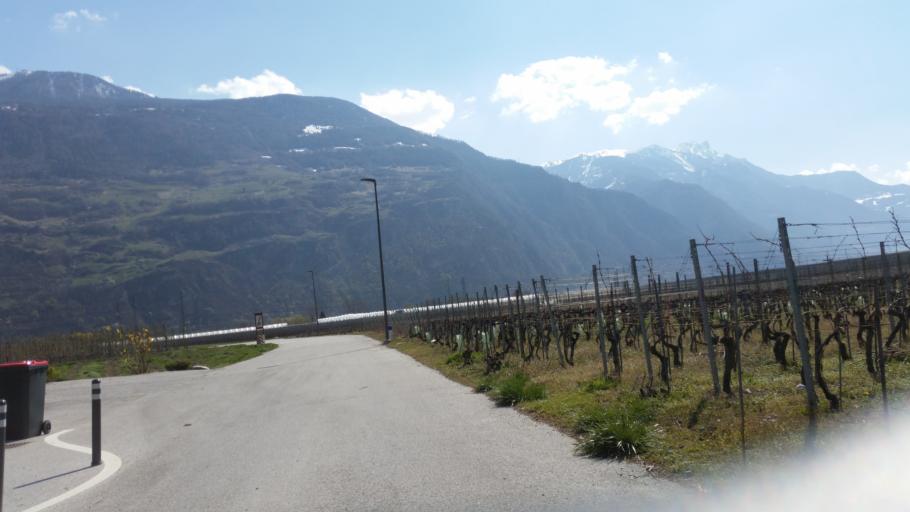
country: CH
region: Valais
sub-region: Conthey District
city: Ardon
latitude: 46.2047
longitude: 7.2544
